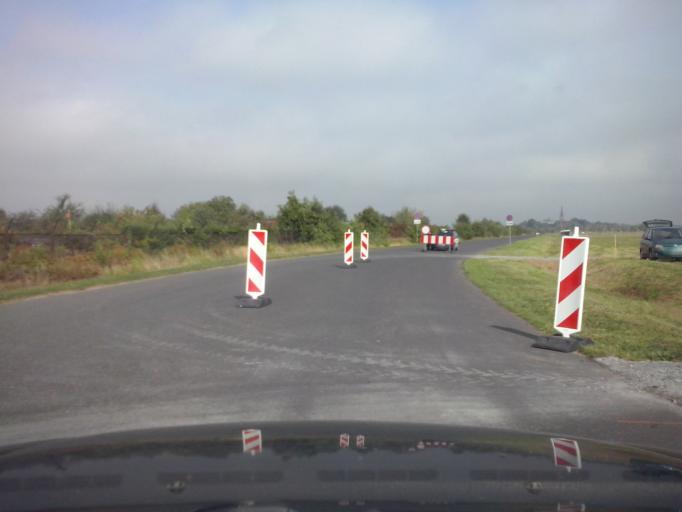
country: PL
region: Subcarpathian Voivodeship
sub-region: Powiat mielecki
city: Mielec
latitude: 50.3187
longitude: 21.4411
